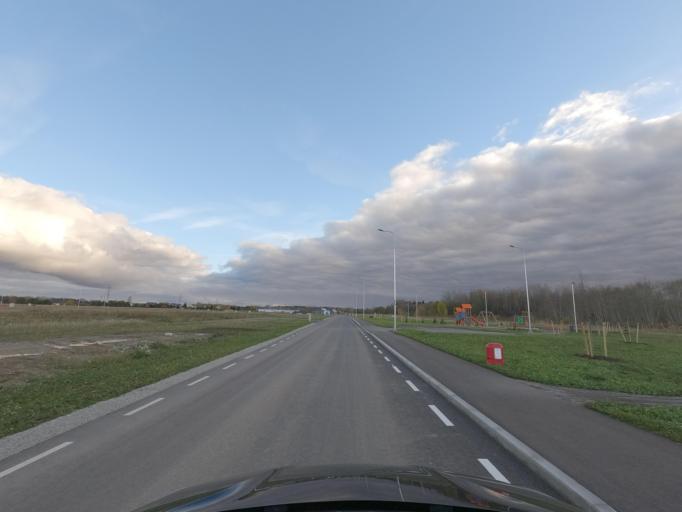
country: EE
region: Harju
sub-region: Saue linn
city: Saue
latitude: 59.3667
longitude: 24.5673
